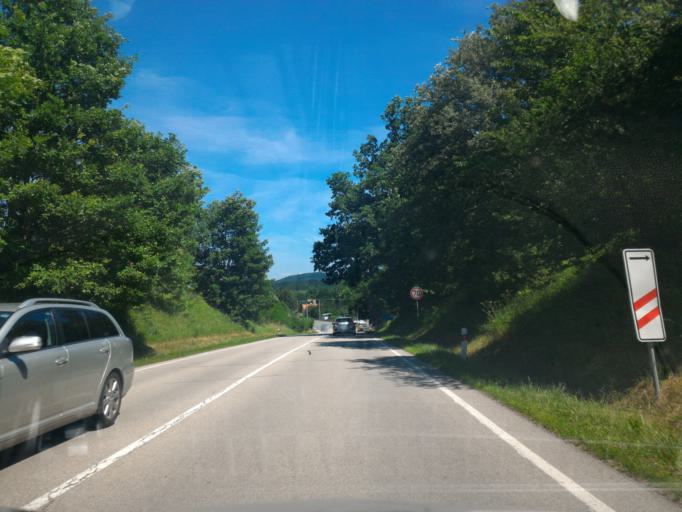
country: CZ
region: Vysocina
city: Dolni Cerekev
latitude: 49.3277
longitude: 15.4829
